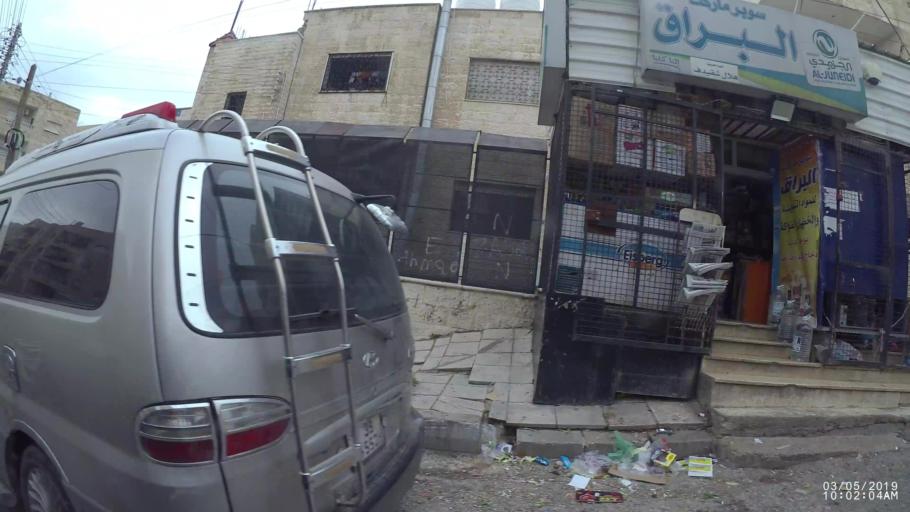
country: JO
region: Amman
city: Amman
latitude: 31.9795
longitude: 35.9295
